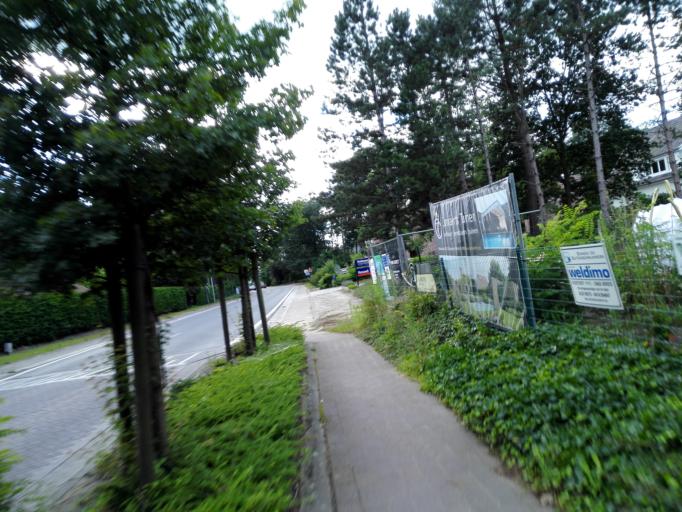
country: BE
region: Flanders
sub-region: Provincie Vlaams-Brabant
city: Keerbergen
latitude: 51.0024
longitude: 4.6398
